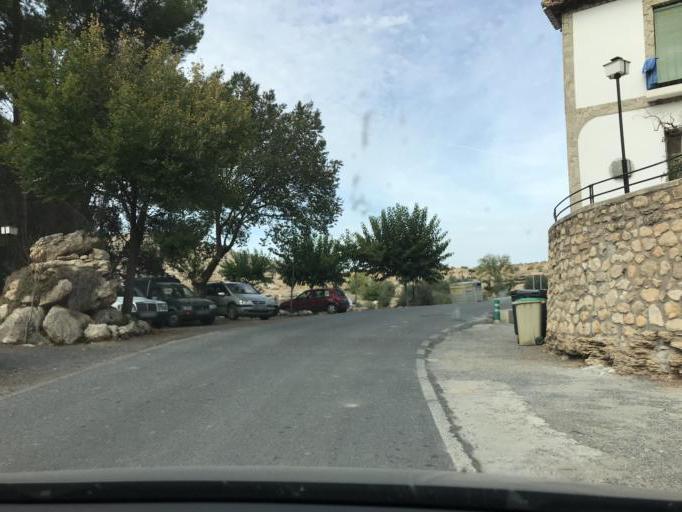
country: ES
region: Andalusia
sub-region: Provincia de Granada
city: Villanueva de las Torres
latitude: 37.5085
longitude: -3.1075
